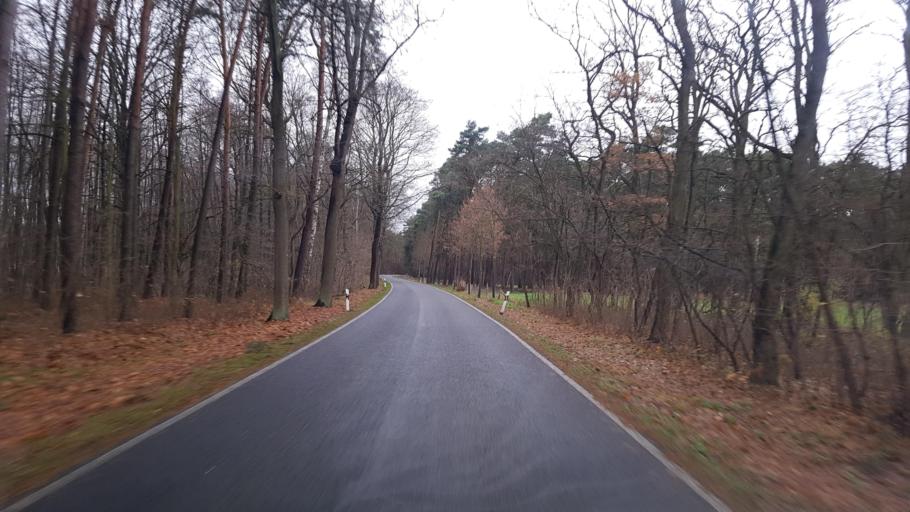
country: DE
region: Brandenburg
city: Tauche
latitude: 52.1010
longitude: 14.1511
